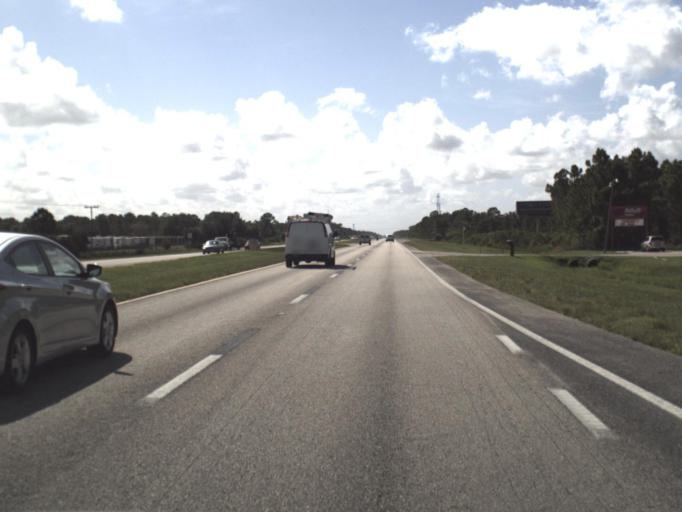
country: US
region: Florida
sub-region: Charlotte County
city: Charlotte Park
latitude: 26.8534
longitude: -81.9849
